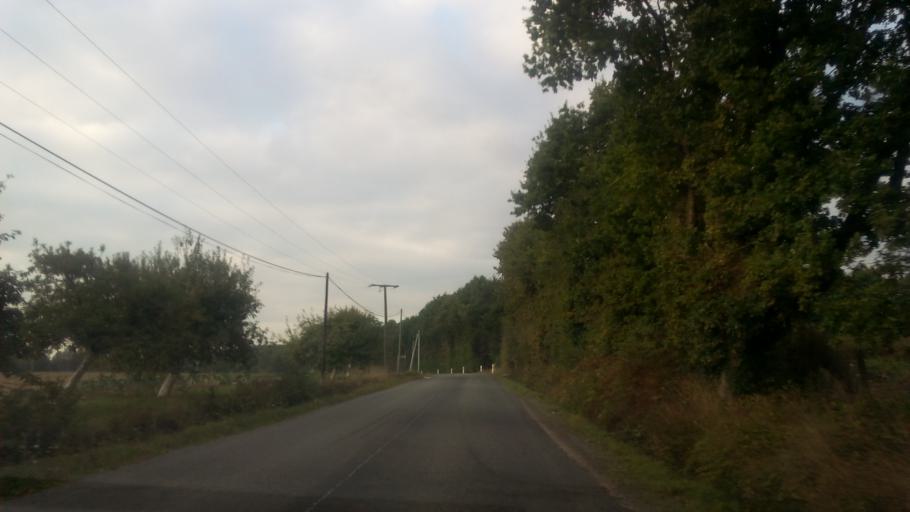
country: FR
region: Brittany
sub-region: Departement du Morbihan
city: Saint-Vincent-sur-Oust
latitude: 47.6758
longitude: -2.1750
